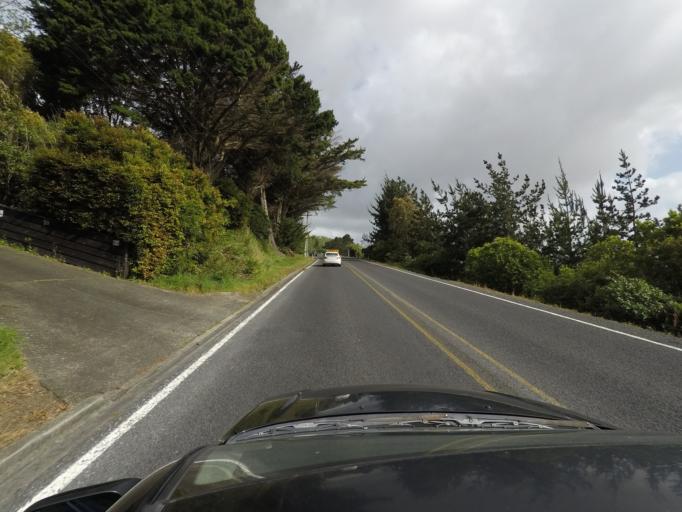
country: NZ
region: Auckland
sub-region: Auckland
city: Pakuranga
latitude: -36.9286
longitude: 174.9358
